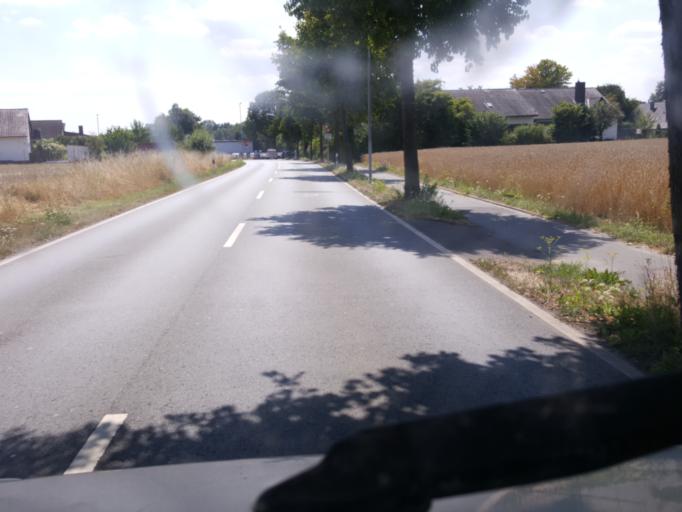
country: DE
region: North Rhine-Westphalia
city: Loehne
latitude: 52.2148
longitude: 8.7211
